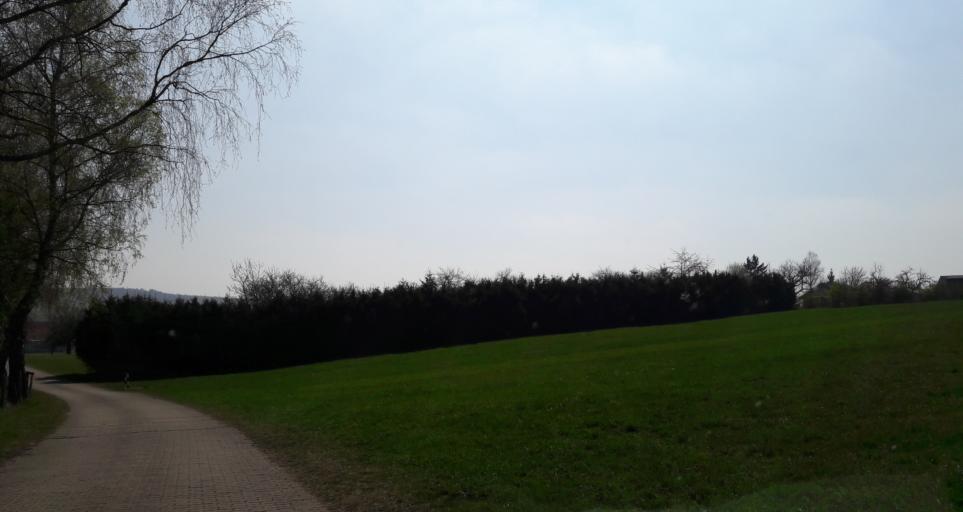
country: DE
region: Saarland
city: Tholey
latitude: 49.5381
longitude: 7.0309
